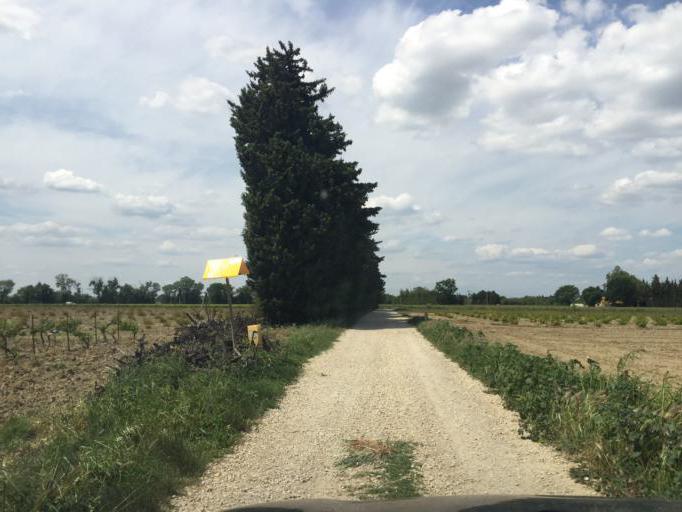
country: FR
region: Provence-Alpes-Cote d'Azur
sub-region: Departement du Vaucluse
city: Jonquieres
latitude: 44.1335
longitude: 4.9064
